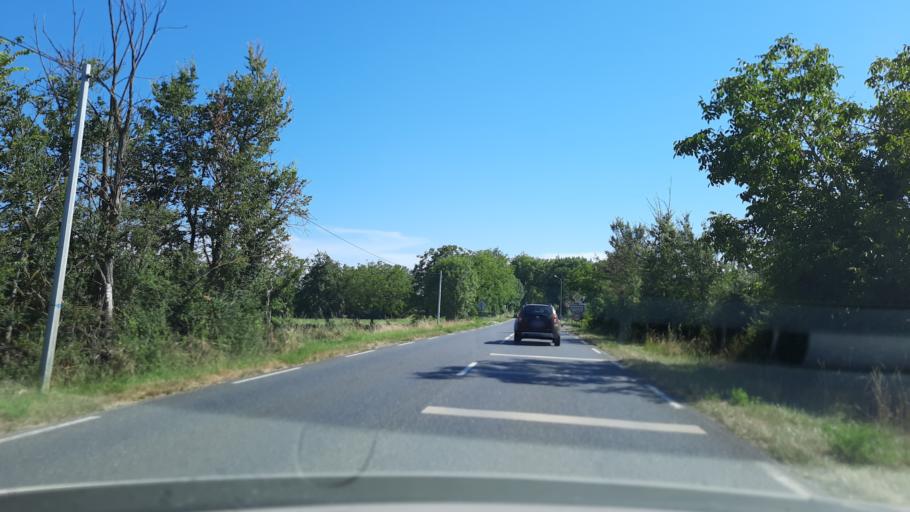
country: FR
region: Midi-Pyrenees
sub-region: Departement du Tarn-et-Garonne
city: Caylus
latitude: 44.3136
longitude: 1.8885
